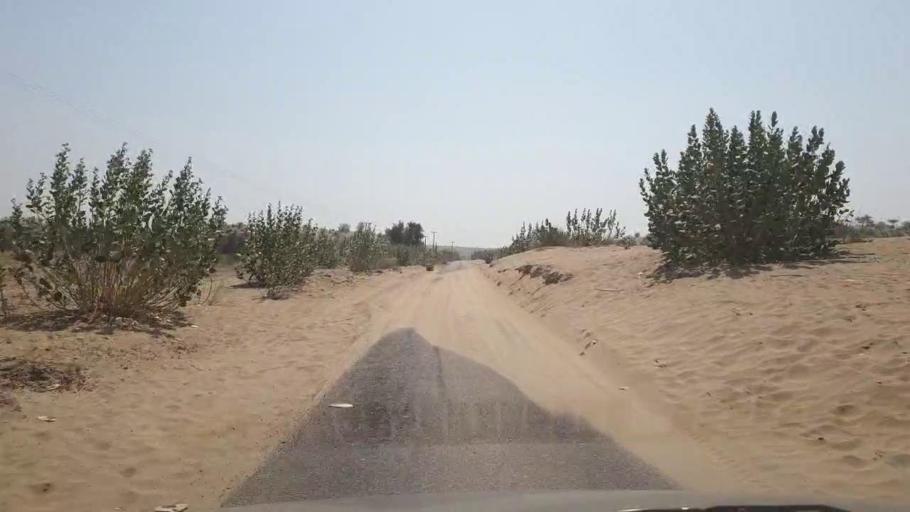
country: PK
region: Sindh
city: Chor
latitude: 25.6472
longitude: 70.1694
